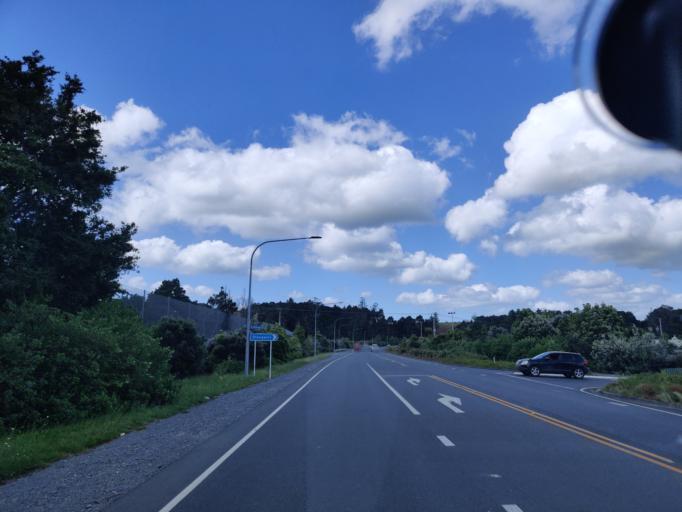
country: NZ
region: Northland
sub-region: Whangarei
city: Whangarei
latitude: -35.6911
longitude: 174.3139
